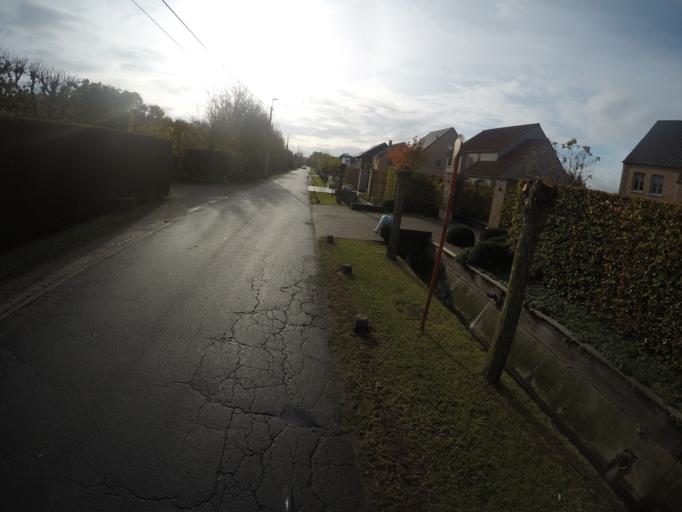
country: BE
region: Flanders
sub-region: Provincie Oost-Vlaanderen
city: Temse
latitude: 51.1559
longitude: 4.1915
